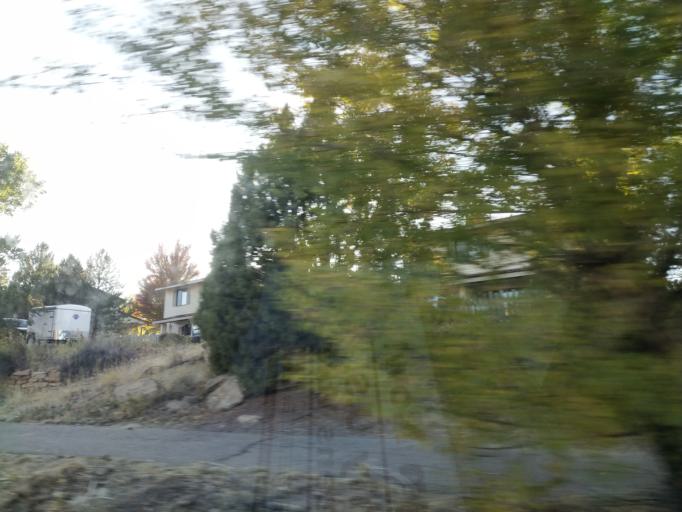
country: US
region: Colorado
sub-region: Mesa County
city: Redlands
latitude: 39.0617
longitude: -108.6088
